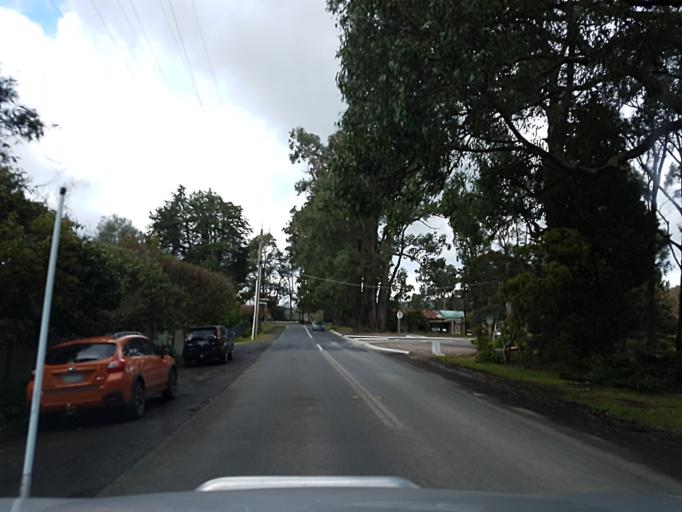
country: AU
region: Victoria
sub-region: Yarra Ranges
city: Monbulk
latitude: -37.8812
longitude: 145.4212
